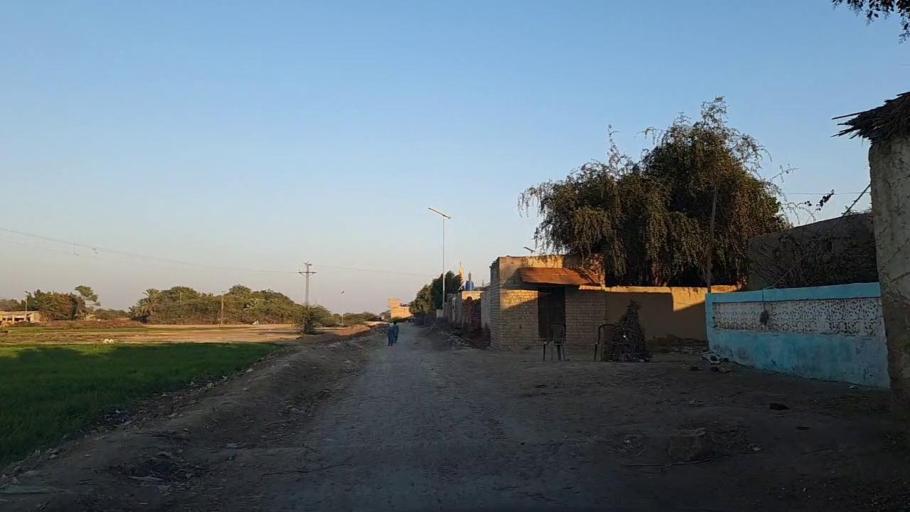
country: PK
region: Sindh
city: Nawabshah
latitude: 26.2483
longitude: 68.3392
